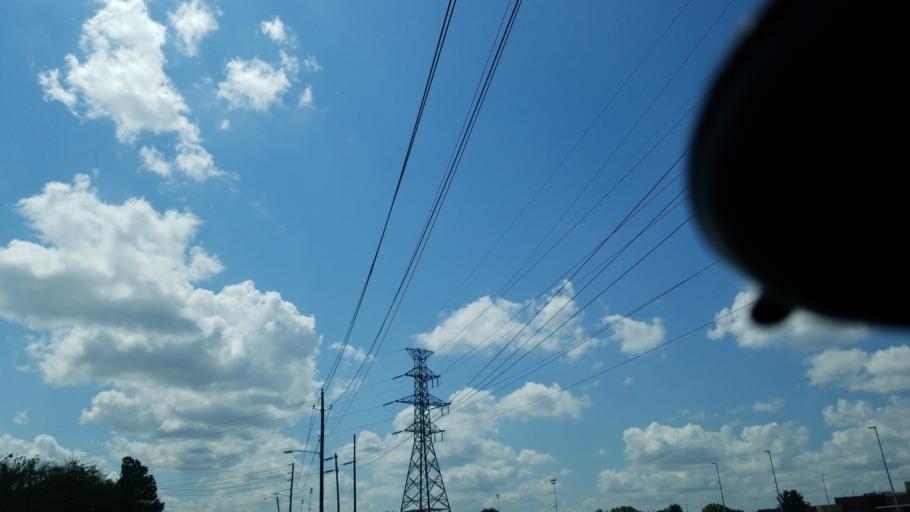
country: US
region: Texas
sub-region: Dallas County
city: Grand Prairie
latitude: 32.7244
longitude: -96.9859
